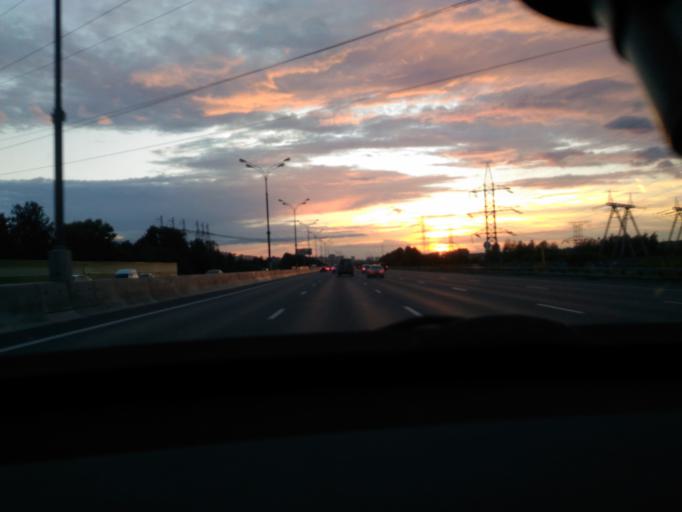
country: RU
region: Moscow
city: Kozeyevo
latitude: 55.8973
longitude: 37.6458
